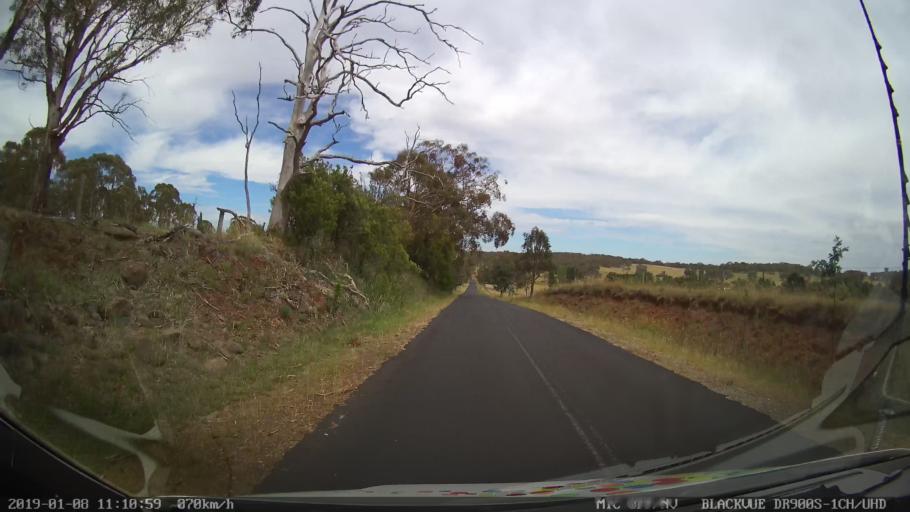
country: AU
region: New South Wales
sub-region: Guyra
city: Guyra
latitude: -30.2266
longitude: 151.6301
